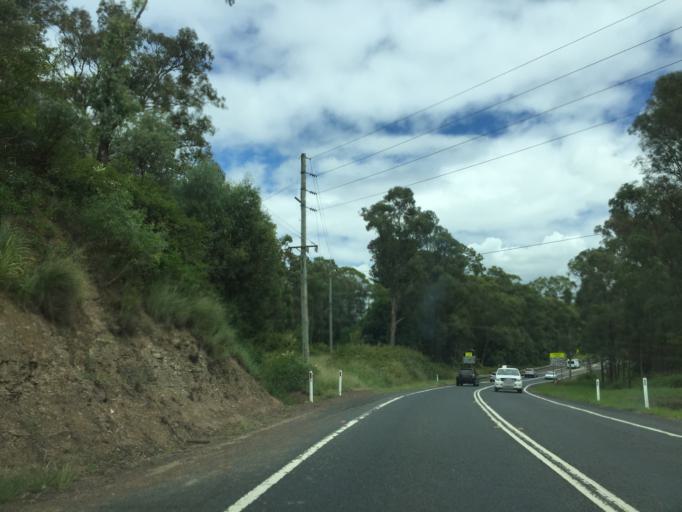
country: AU
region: New South Wales
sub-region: Hawkesbury
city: Richmond
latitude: -33.5719
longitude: 150.7089
